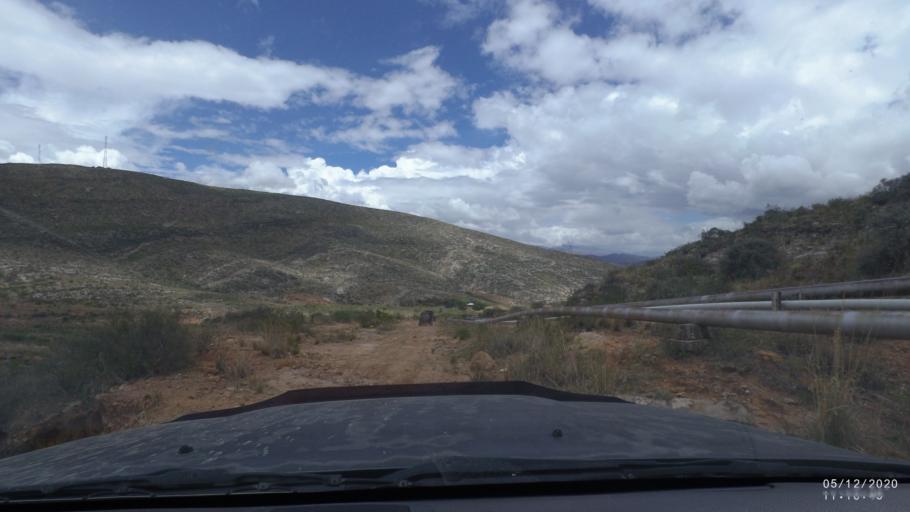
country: BO
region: Cochabamba
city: Sipe Sipe
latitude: -17.5502
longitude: -66.3197
